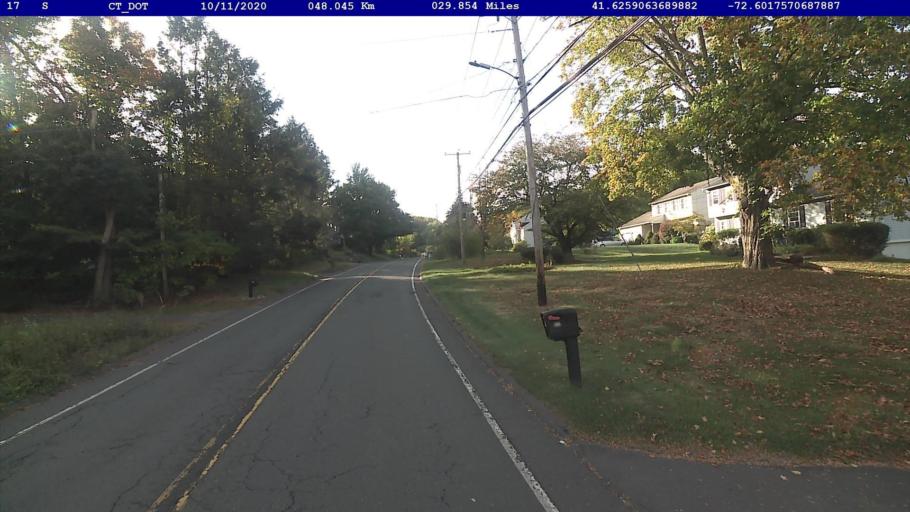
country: US
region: Connecticut
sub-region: Middlesex County
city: Cromwell
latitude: 41.6259
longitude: -72.6018
